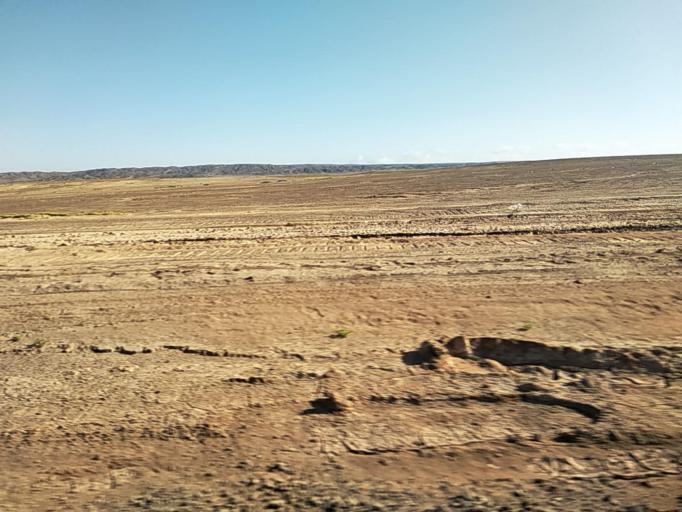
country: CL
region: Atacama
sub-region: Provincia de Copiapo
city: Copiapo
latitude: -27.3304
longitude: -70.7919
